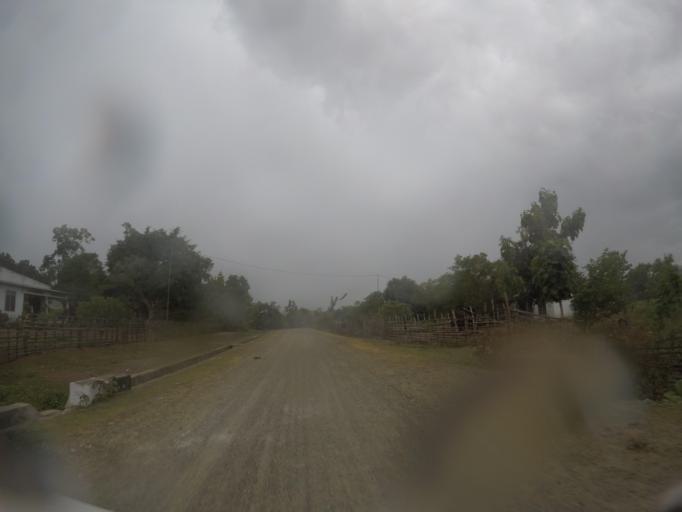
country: TL
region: Bobonaro
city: Maliana
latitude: -8.8554
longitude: 125.0857
